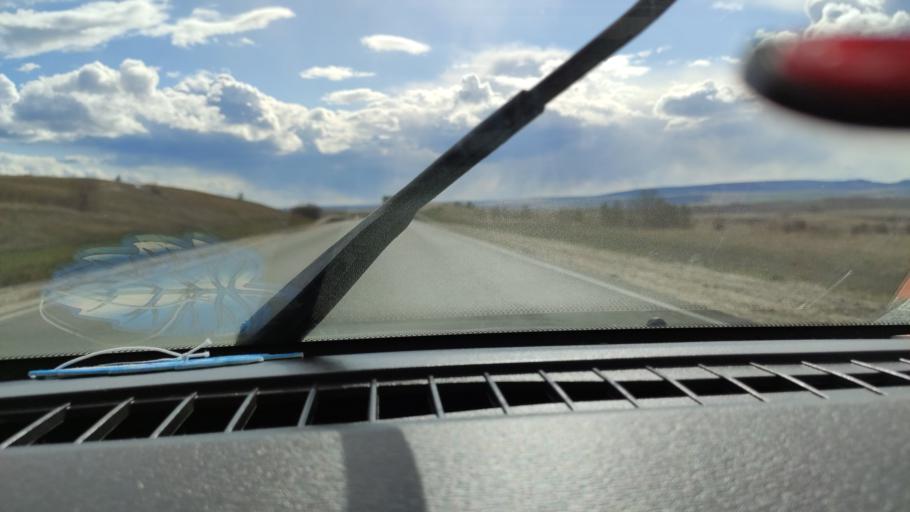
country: RU
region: Saratov
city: Alekseyevka
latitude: 52.3534
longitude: 47.9432
